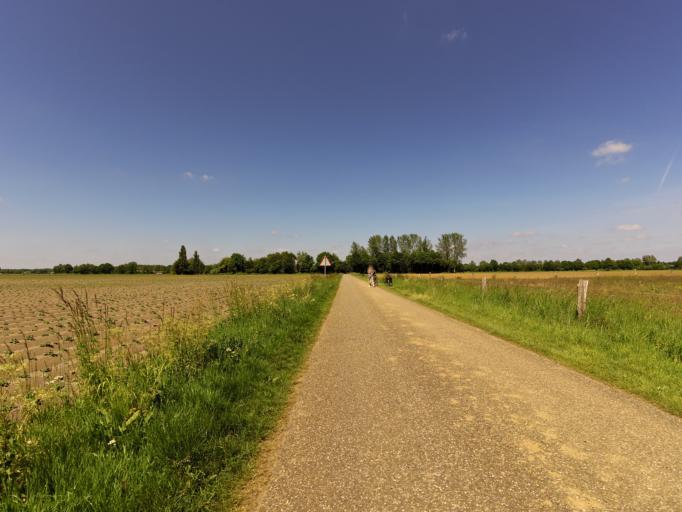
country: NL
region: Gelderland
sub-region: Gemeente Bronckhorst
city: Hengelo
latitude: 52.0710
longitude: 6.2907
